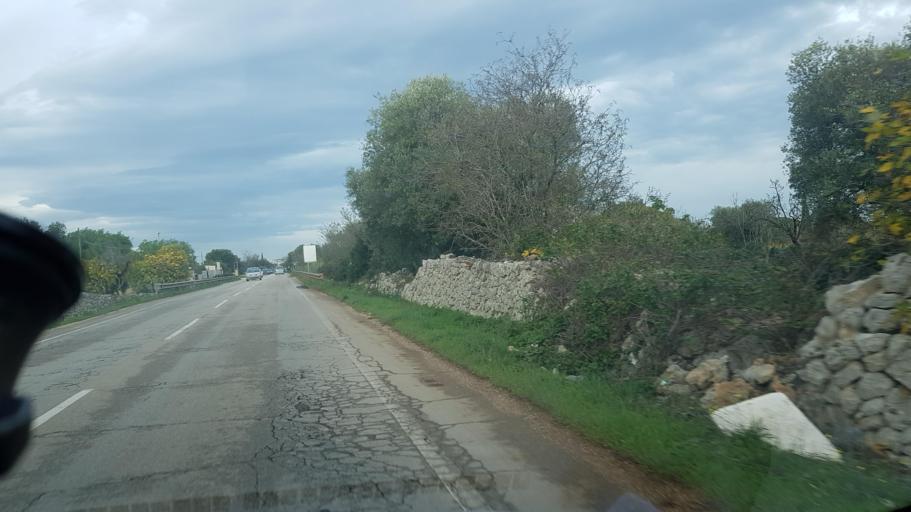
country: IT
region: Apulia
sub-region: Provincia di Brindisi
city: San Vito dei Normanni
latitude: 40.6758
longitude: 17.6887
